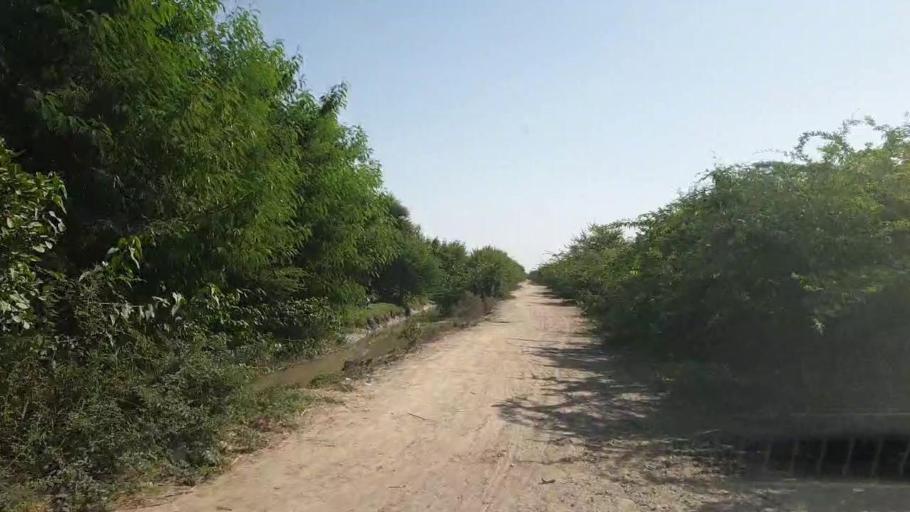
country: PK
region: Sindh
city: Kadhan
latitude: 24.5890
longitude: 69.0090
